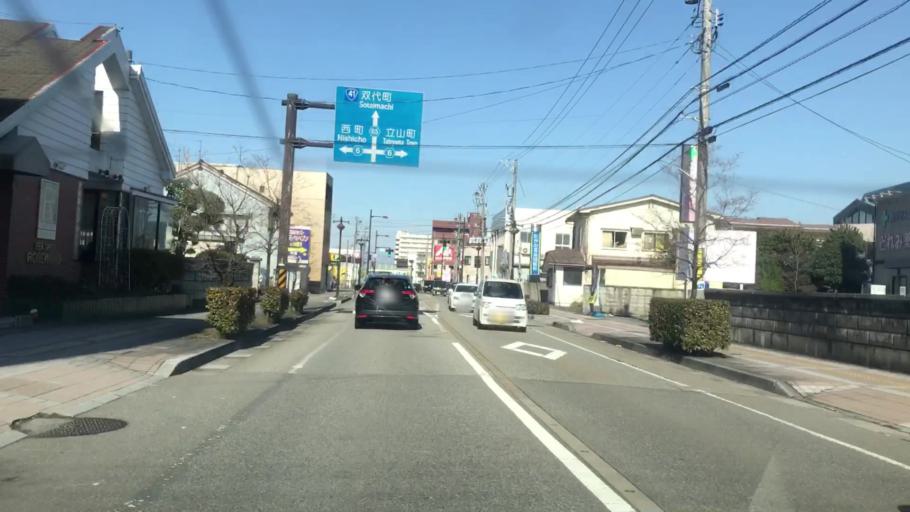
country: JP
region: Toyama
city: Toyama-shi
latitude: 36.6867
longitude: 137.2363
